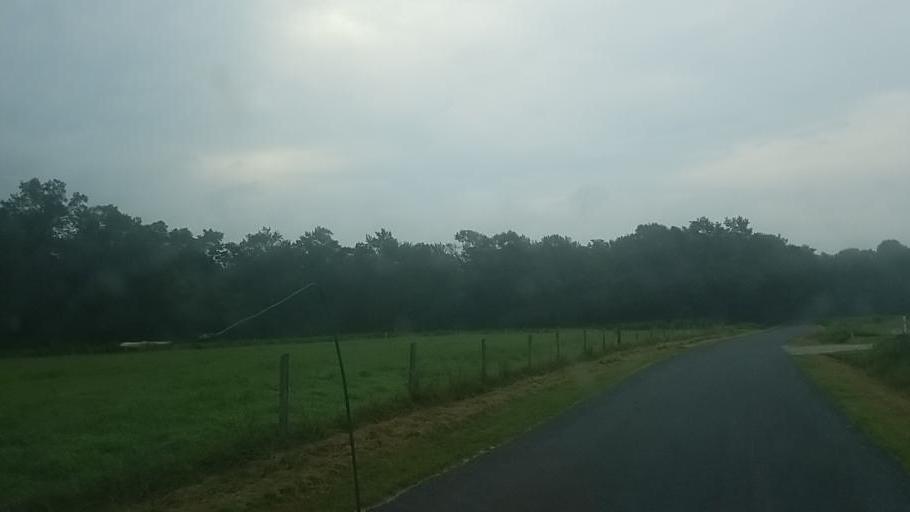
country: US
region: Maryland
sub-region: Wicomico County
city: Pittsville
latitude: 38.4439
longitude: -75.3431
